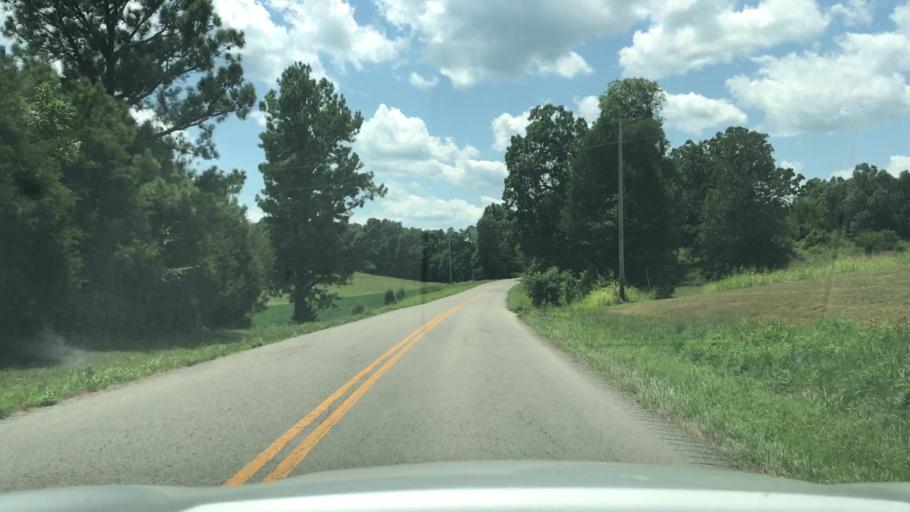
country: US
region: Kentucky
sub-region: Muhlenberg County
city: Greenville
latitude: 37.1384
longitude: -87.2653
